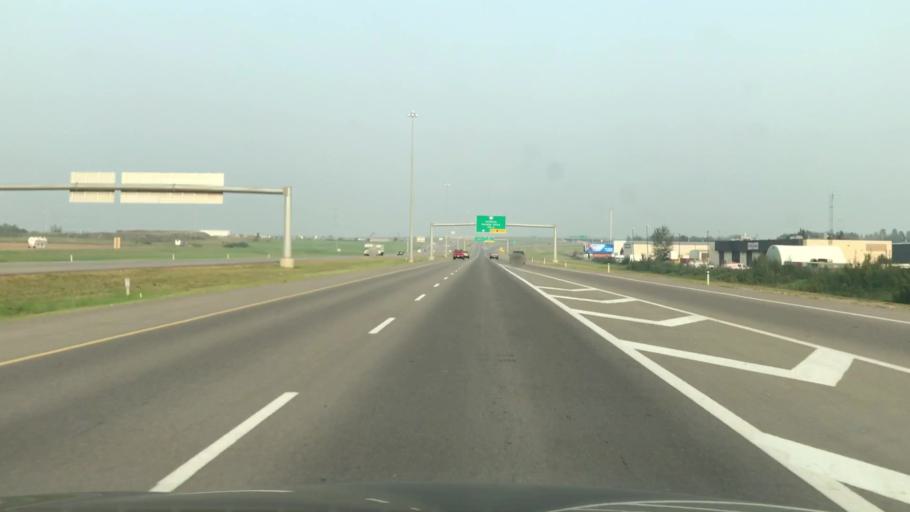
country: CA
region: Alberta
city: Sherwood Park
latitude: 53.5161
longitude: -113.3641
